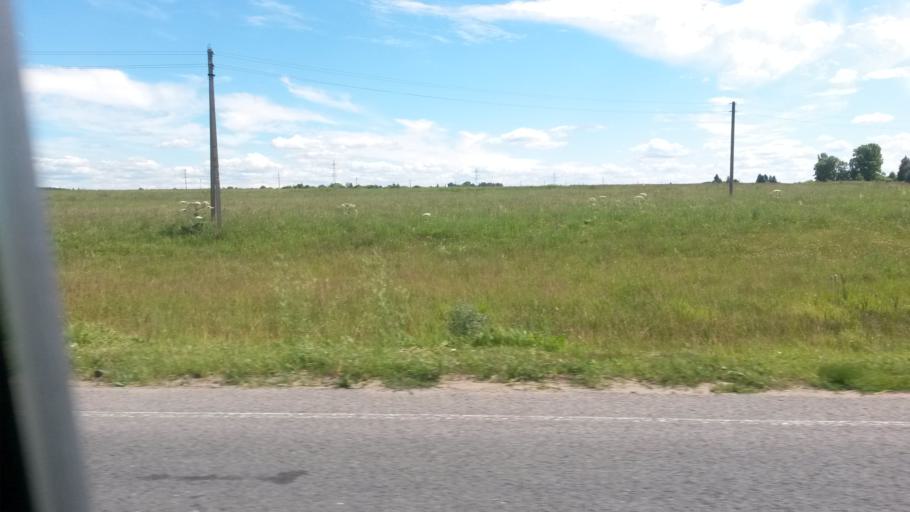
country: RU
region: Ivanovo
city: Staraya Vichuga
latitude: 57.2377
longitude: 41.8819
